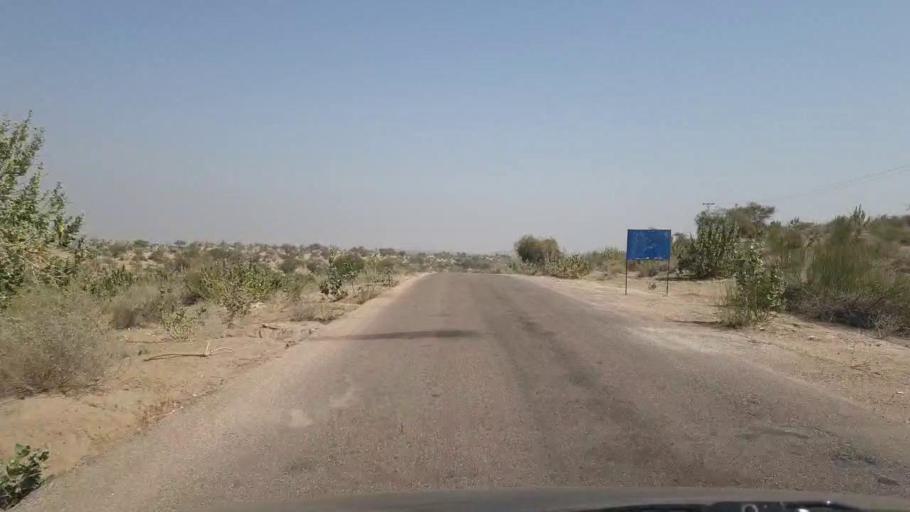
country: PK
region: Sindh
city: Chor
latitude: 25.6376
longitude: 70.0798
